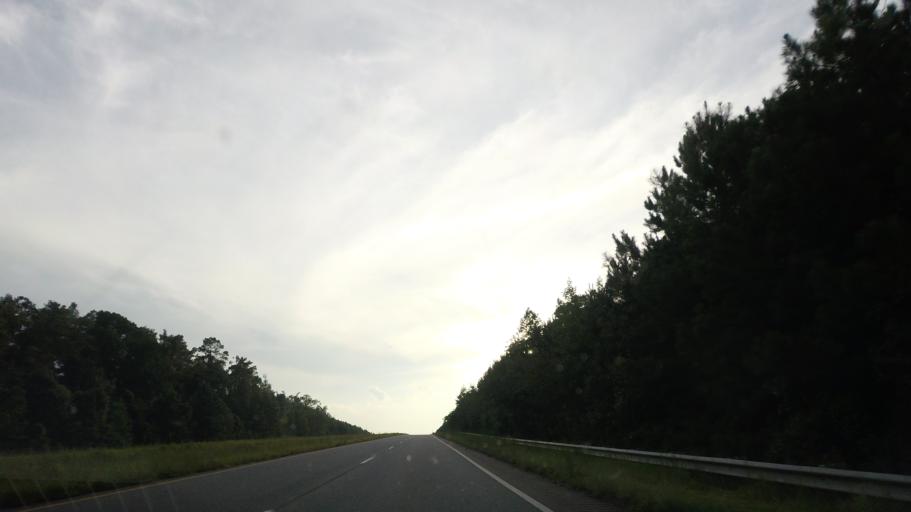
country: US
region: Georgia
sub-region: Wilkinson County
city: Gordon
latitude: 32.8555
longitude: -83.3905
